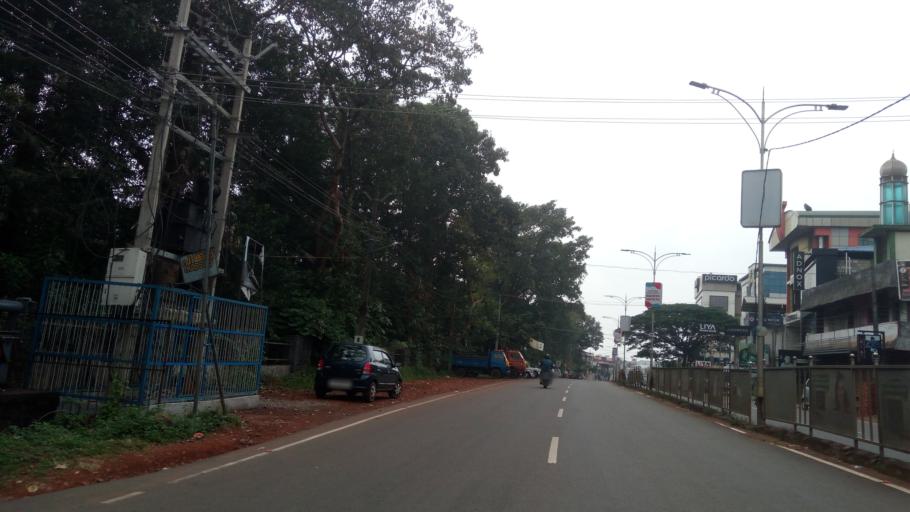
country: IN
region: Kerala
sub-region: Malappuram
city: Malappuram
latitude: 11.0000
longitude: 75.9998
